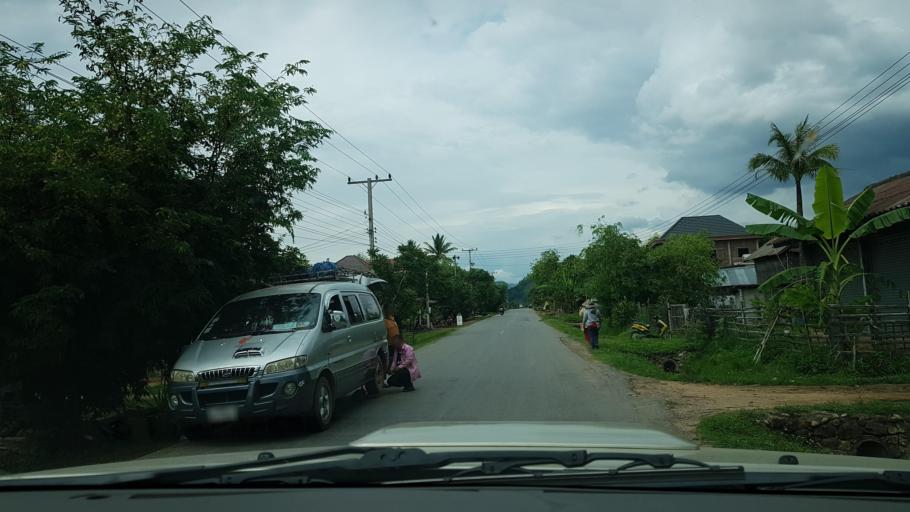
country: LA
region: Loungnamtha
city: Muang Nale
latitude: 20.3286
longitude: 101.6675
